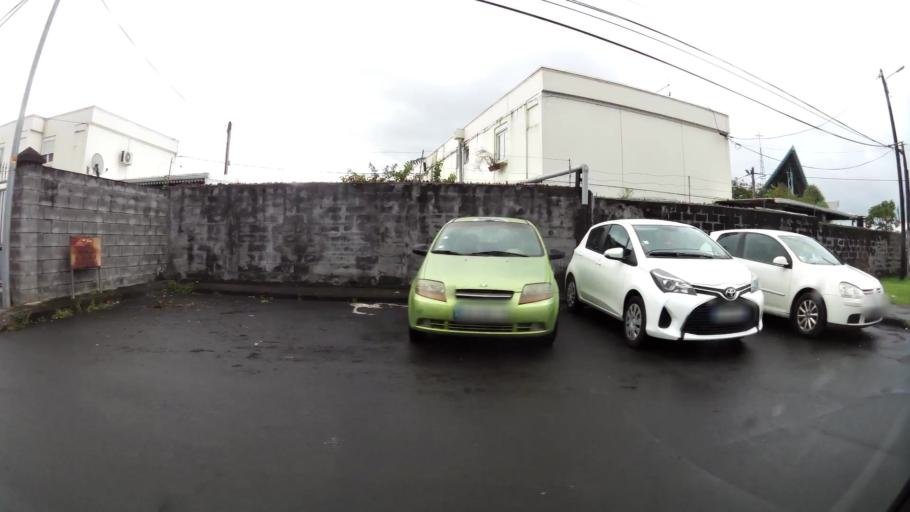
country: RE
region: Reunion
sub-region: Reunion
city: Saint-Andre
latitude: -20.9332
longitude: 55.6510
